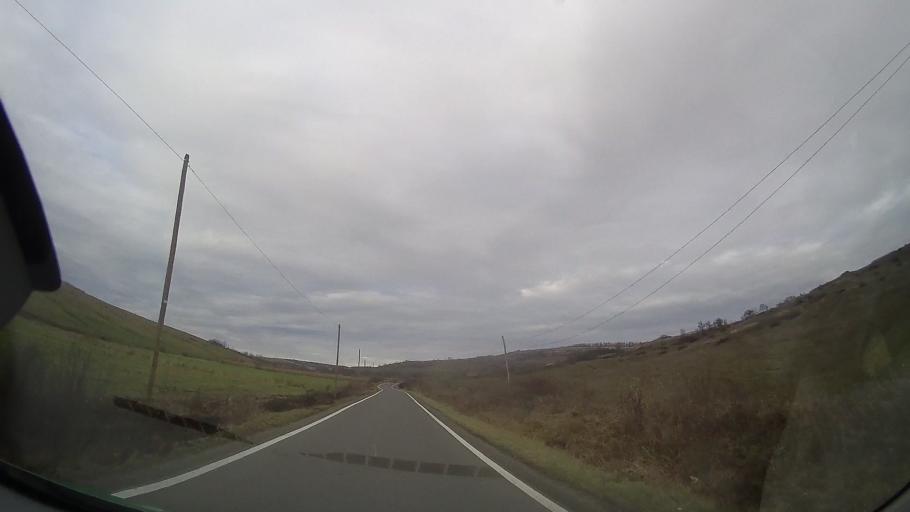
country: RO
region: Mures
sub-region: Comuna Cozma
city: Cozma
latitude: 46.7976
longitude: 24.5393
